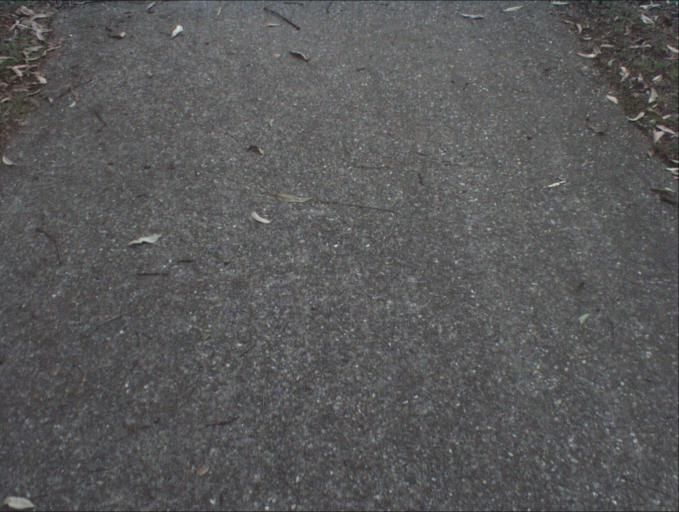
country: AU
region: Queensland
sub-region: Logan
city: Park Ridge South
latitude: -27.6780
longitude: 153.0186
